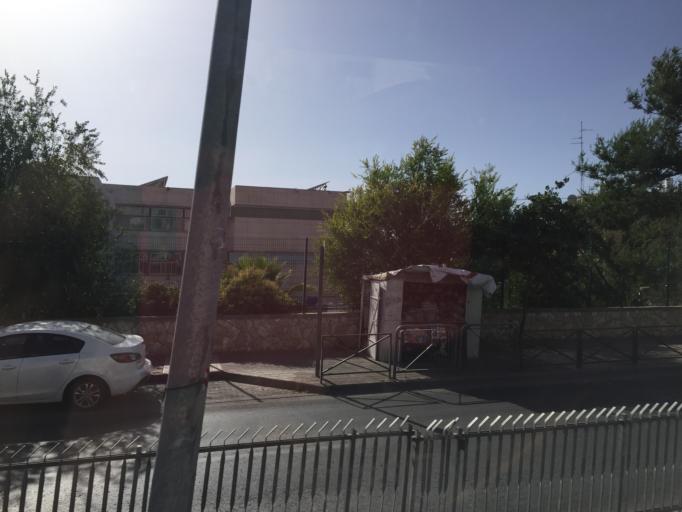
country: IL
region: Jerusalem
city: Jerusalem
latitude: 31.7487
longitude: 35.2183
